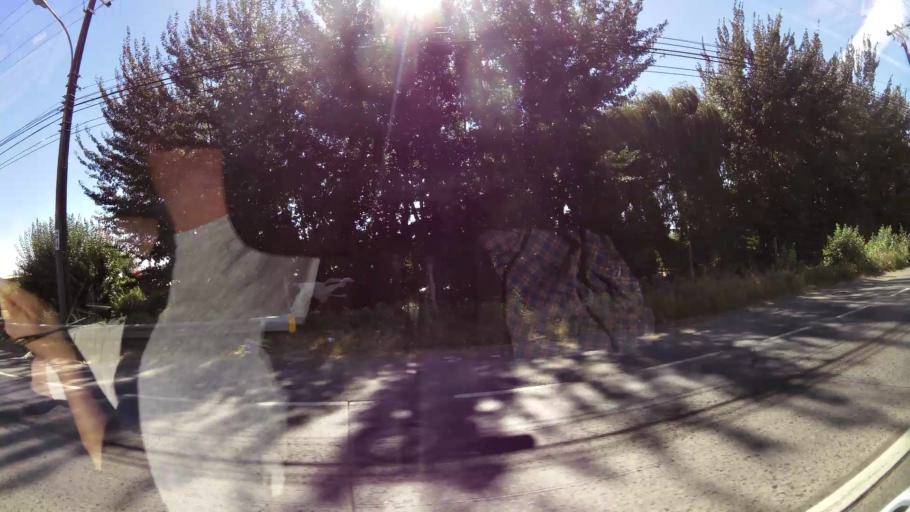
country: CL
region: Biobio
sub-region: Provincia de Concepcion
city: Concepcion
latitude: -36.7884
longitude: -73.0238
